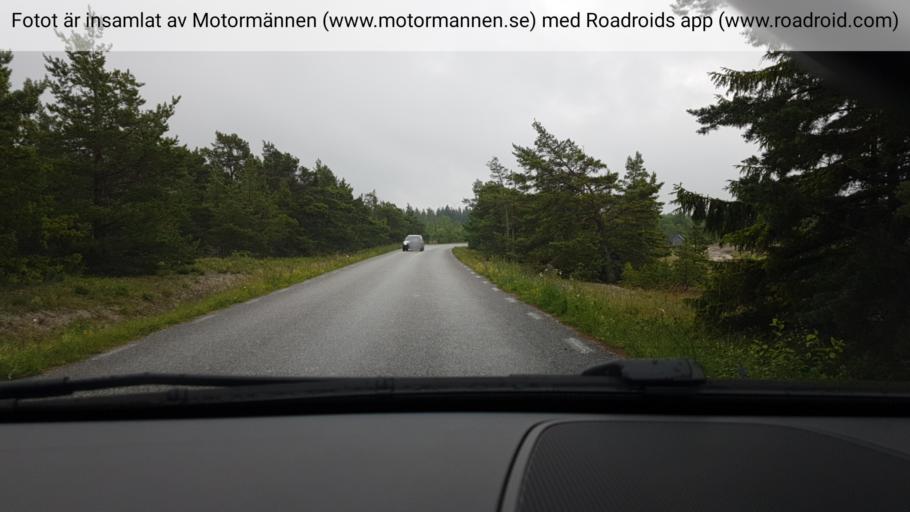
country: SE
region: Gotland
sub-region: Gotland
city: Slite
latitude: 57.8521
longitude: 18.8098
